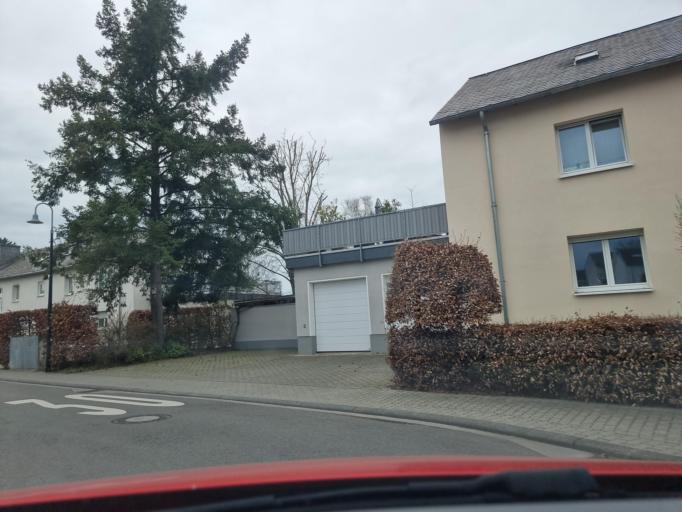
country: DE
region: Rheinland-Pfalz
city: Trier
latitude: 49.7321
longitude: 6.6343
